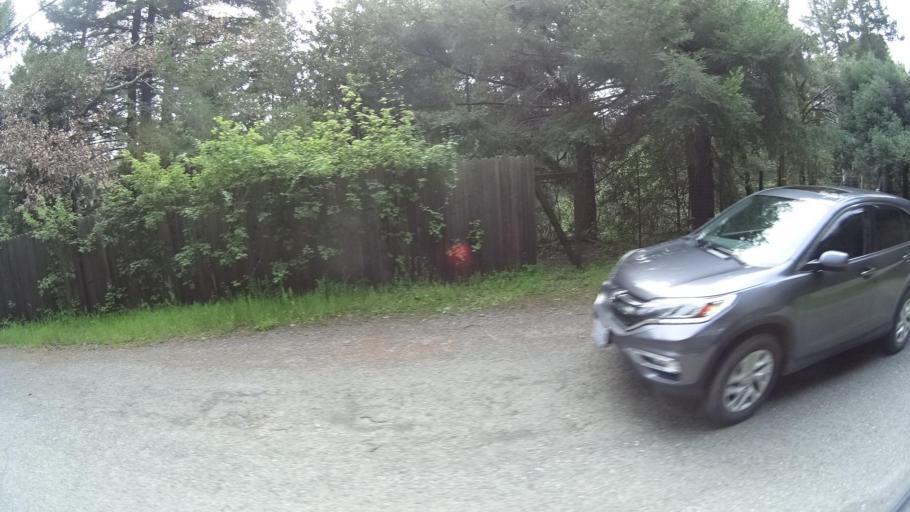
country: US
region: California
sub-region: Humboldt County
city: Redway
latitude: 40.2453
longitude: -123.8332
